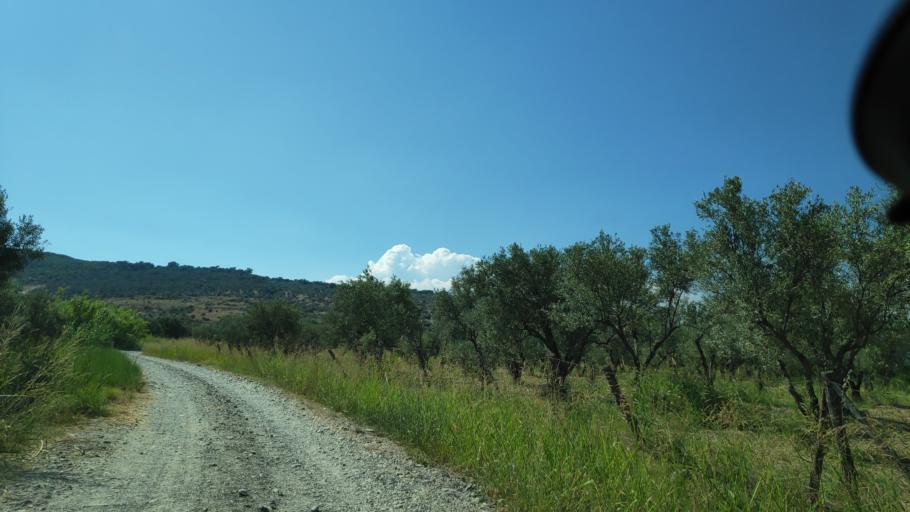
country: IT
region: Calabria
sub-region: Provincia di Reggio Calabria
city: Monasterace
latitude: 38.4358
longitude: 16.5292
